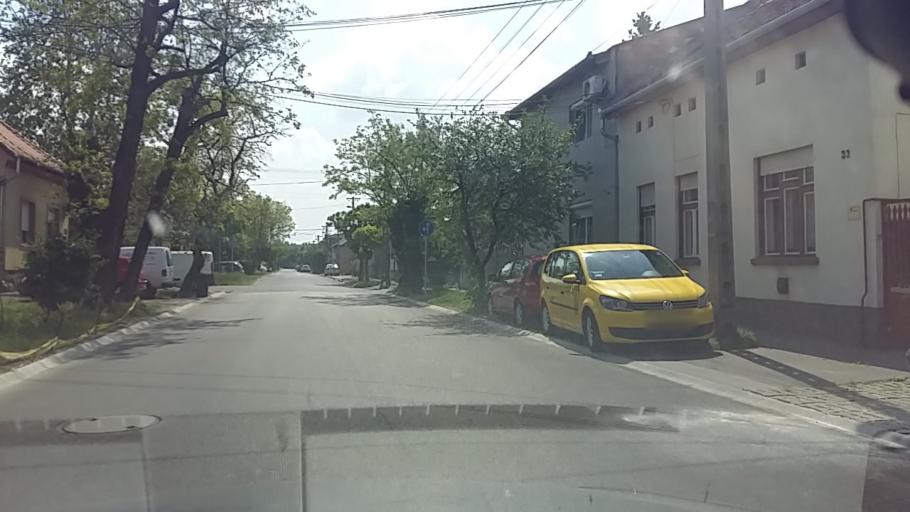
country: HU
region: Budapest
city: Budapest XV. keruelet
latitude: 47.5600
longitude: 19.1268
